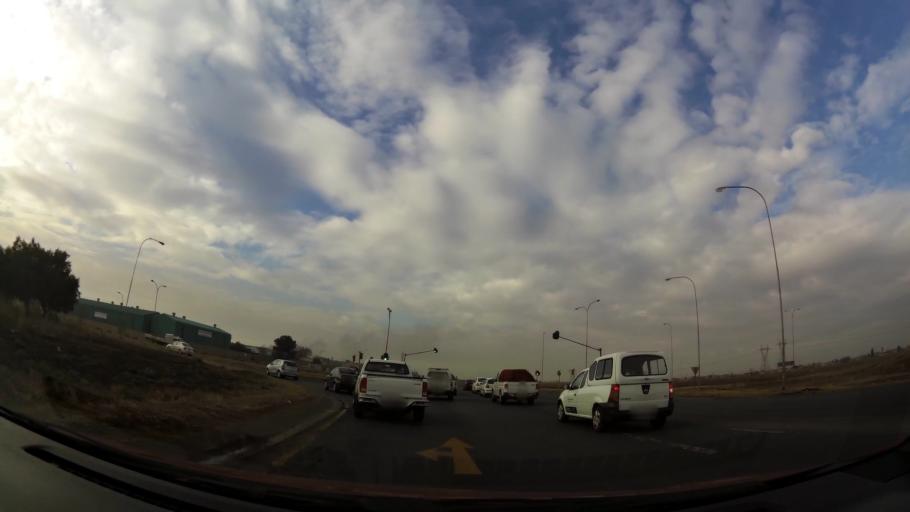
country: ZA
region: Gauteng
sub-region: Sedibeng District Municipality
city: Vanderbijlpark
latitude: -26.6768
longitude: 27.7932
